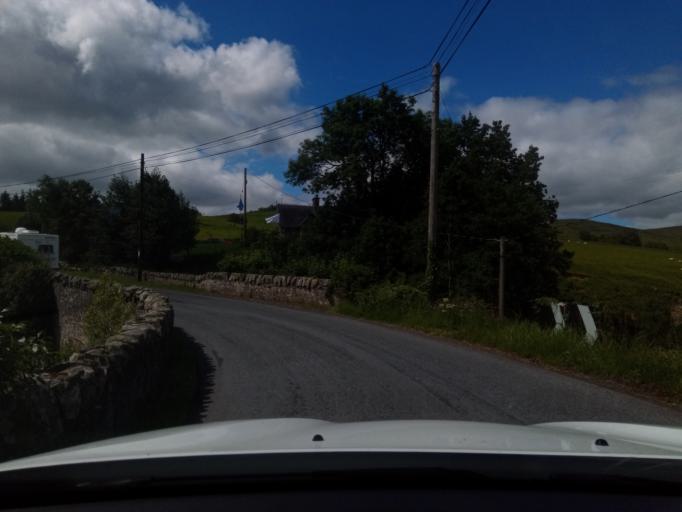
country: GB
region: Scotland
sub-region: The Scottish Borders
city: Innerleithen
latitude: 55.5551
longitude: -2.9705
